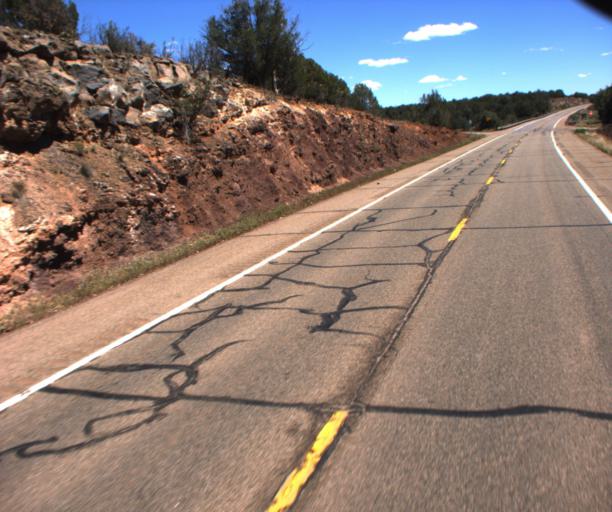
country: US
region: Arizona
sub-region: Yavapai County
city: Paulden
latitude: 35.0831
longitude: -112.4065
